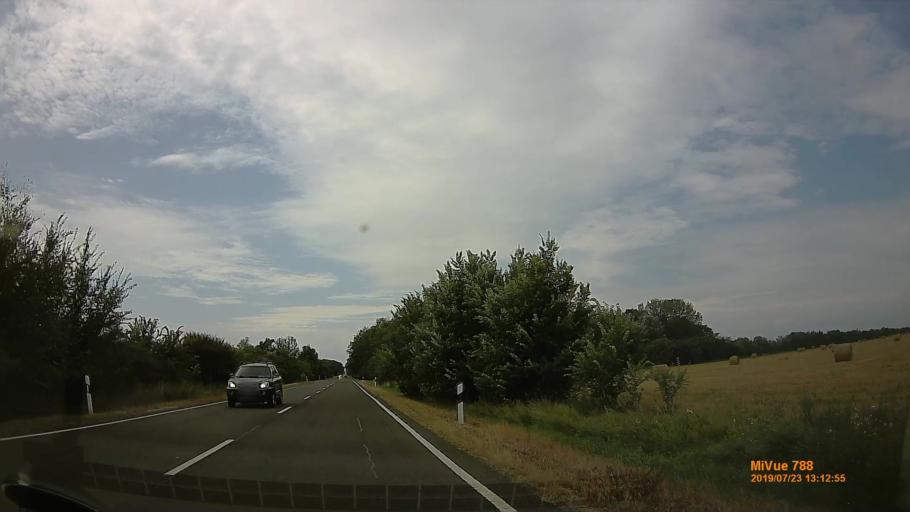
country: HU
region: Hajdu-Bihar
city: Gorbehaza
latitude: 47.9279
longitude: 21.2418
